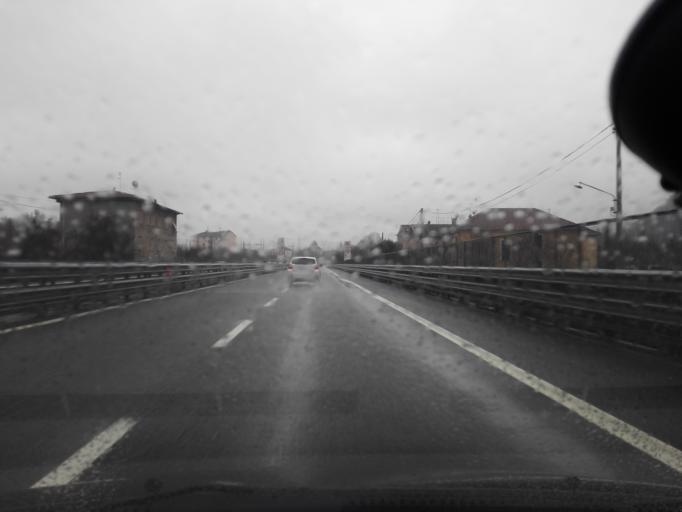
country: IT
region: Piedmont
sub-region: Provincia di Alessandria
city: Serravalle Scrivia
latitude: 44.7188
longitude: 8.8636
